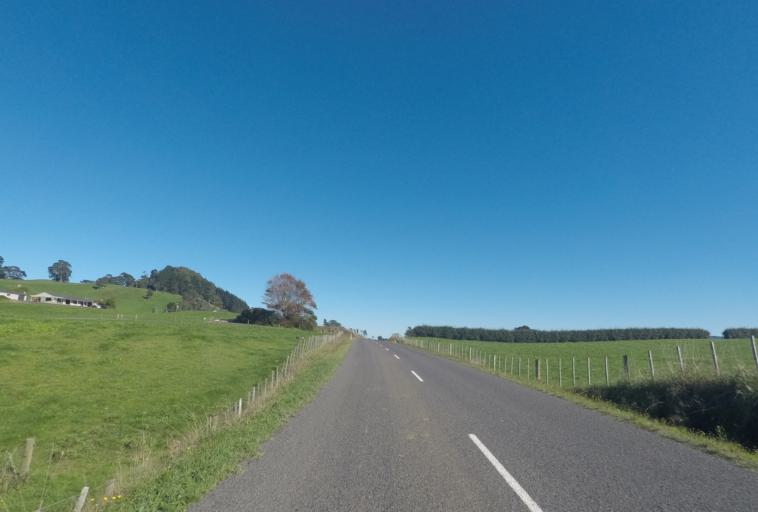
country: NZ
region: Bay of Plenty
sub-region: Western Bay of Plenty District
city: Waihi Beach
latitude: -37.3879
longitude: 175.9024
